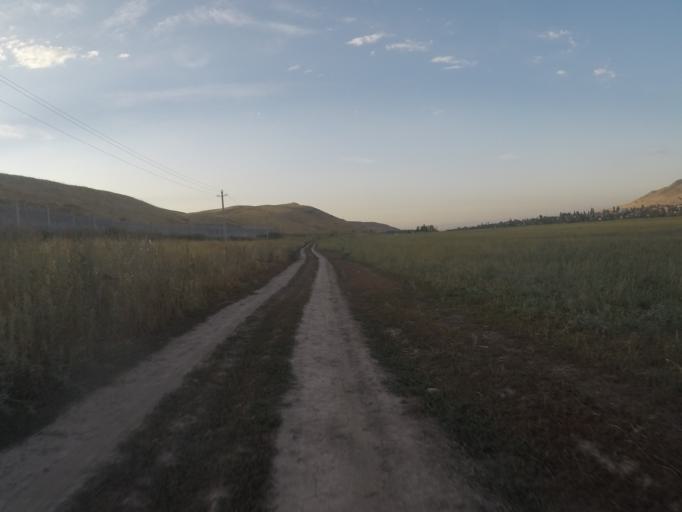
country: KG
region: Chuy
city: Bishkek
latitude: 42.7577
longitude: 74.6361
